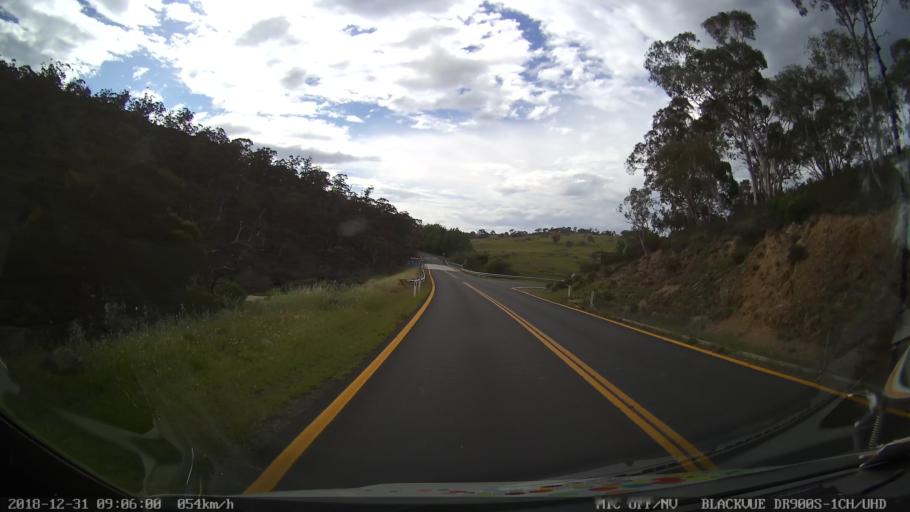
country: AU
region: New South Wales
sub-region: Snowy River
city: Jindabyne
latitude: -36.3685
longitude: 148.5893
